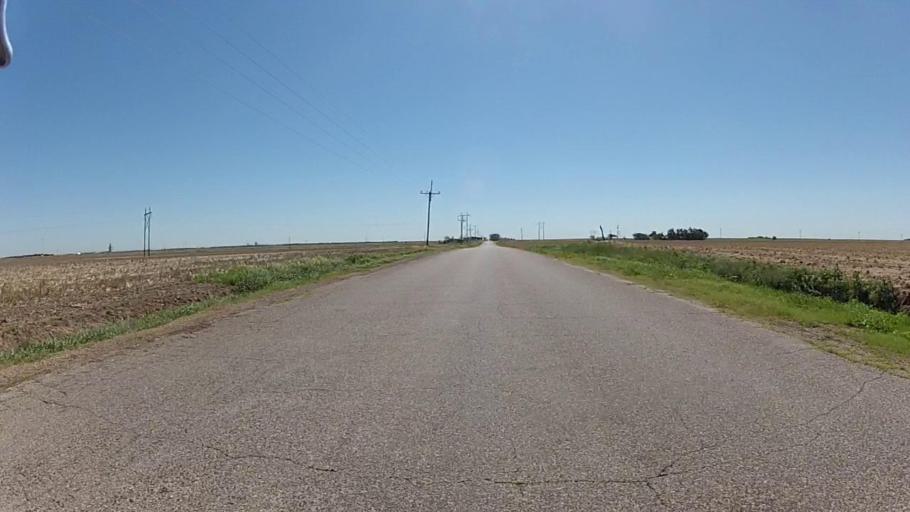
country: US
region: Kansas
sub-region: Kiowa County
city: Greensburg
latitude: 37.5866
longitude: -99.3431
